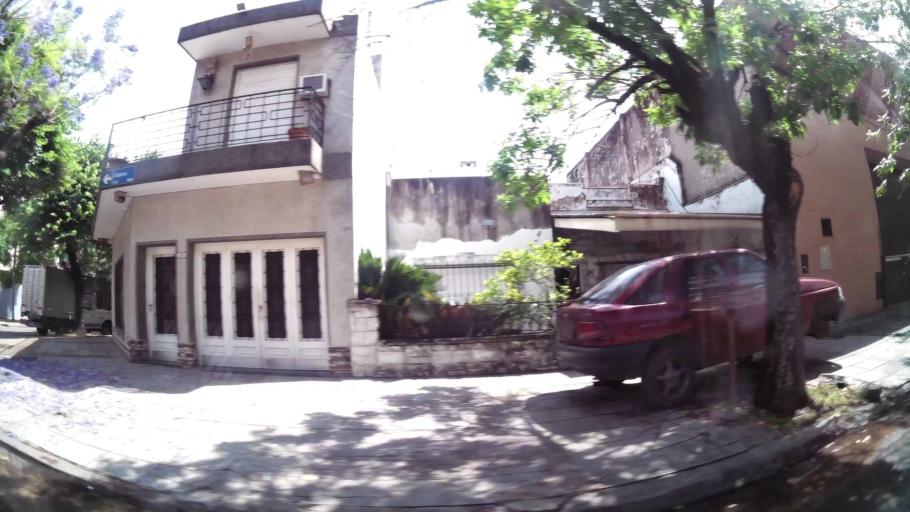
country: AR
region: Buenos Aires F.D.
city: Villa Lugano
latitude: -34.6644
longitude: -58.4318
